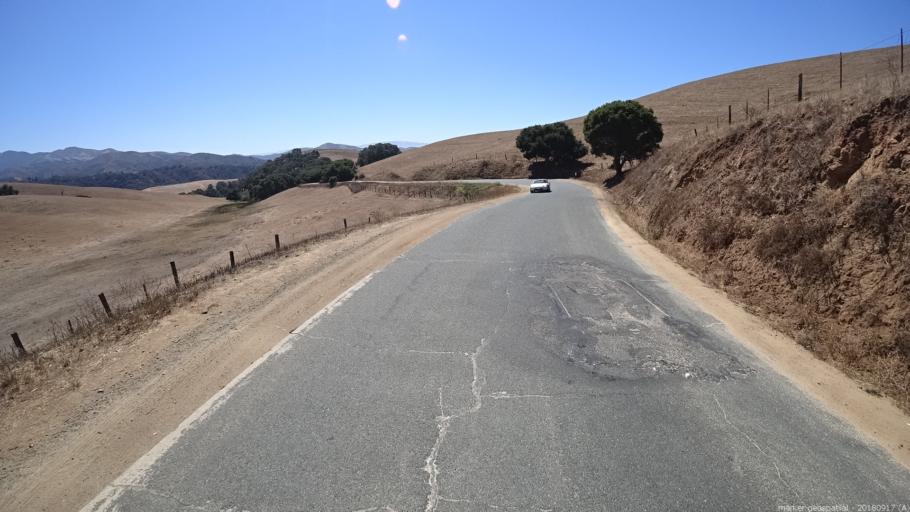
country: US
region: California
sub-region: San Benito County
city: San Juan Bautista
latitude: 36.8088
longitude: -121.5828
